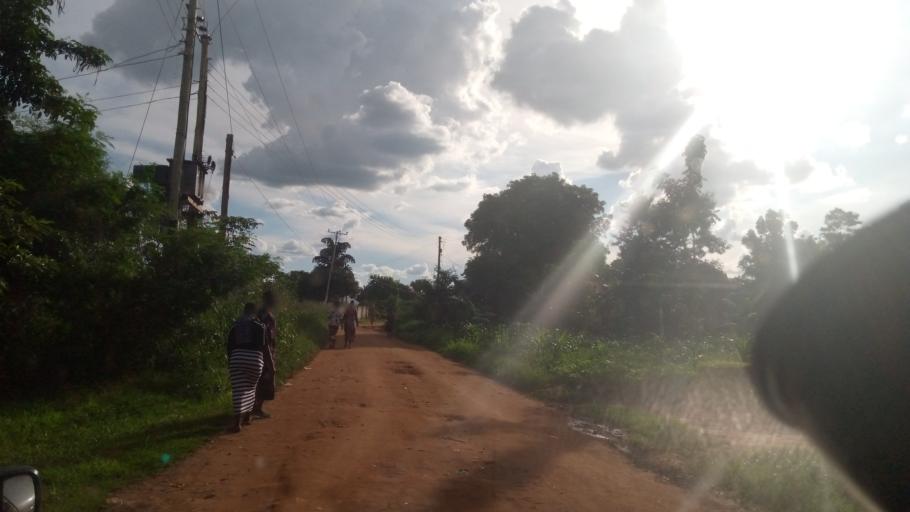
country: UG
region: Northern Region
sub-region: Lira District
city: Lira
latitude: 2.2263
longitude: 32.8908
